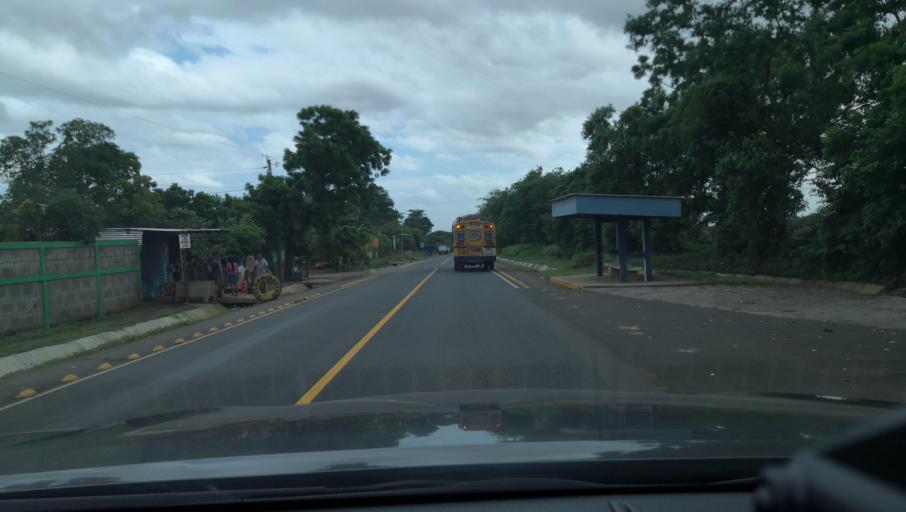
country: NI
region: Masaya
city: Nindiri
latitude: 12.0491
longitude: -86.1335
